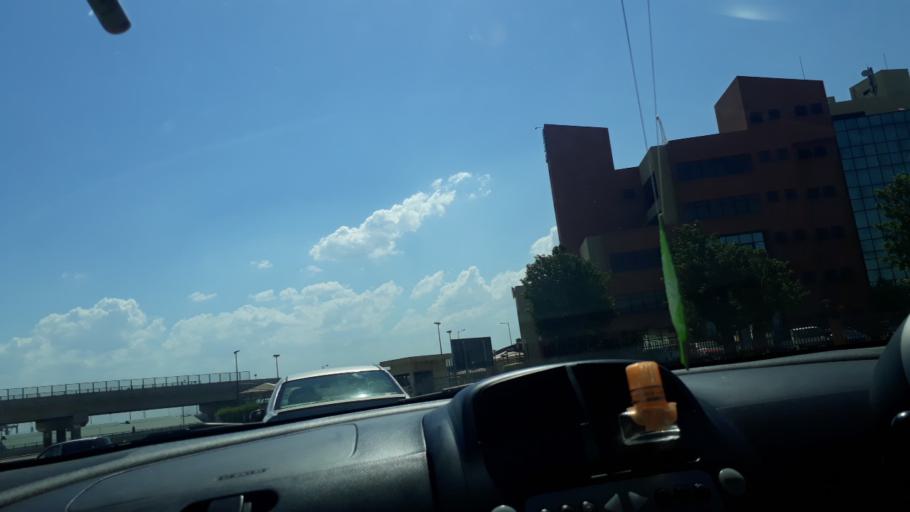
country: MZ
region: Maputo City
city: Maputo
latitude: -25.9541
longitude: 32.5527
